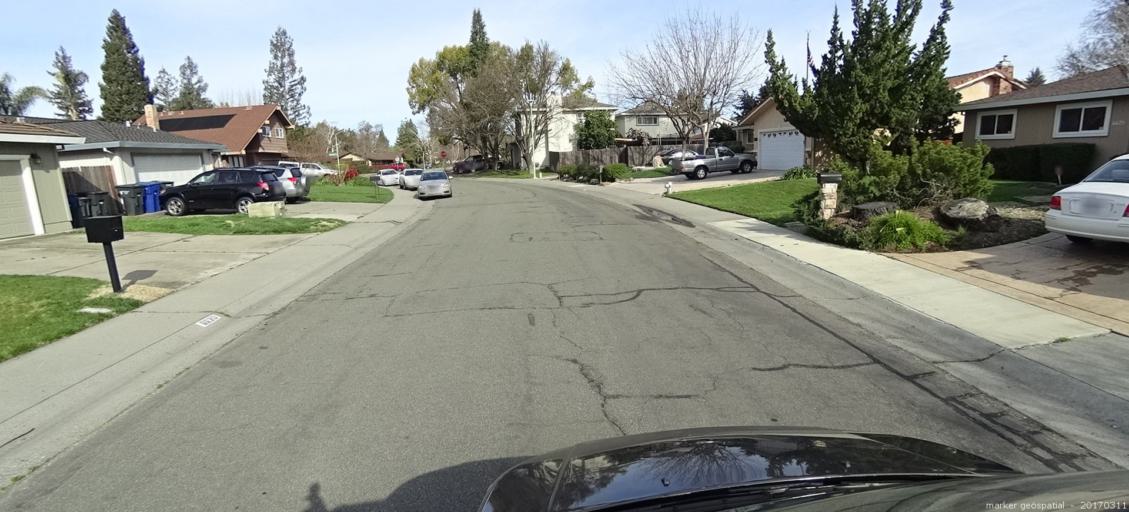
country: US
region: California
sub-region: Yolo County
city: West Sacramento
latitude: 38.5071
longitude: -121.5466
